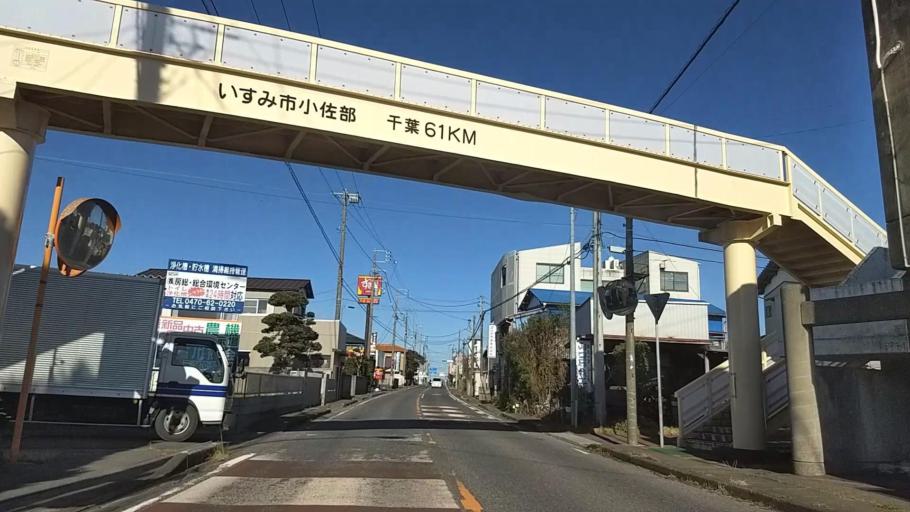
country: JP
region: Chiba
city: Ohara
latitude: 35.2461
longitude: 140.3940
